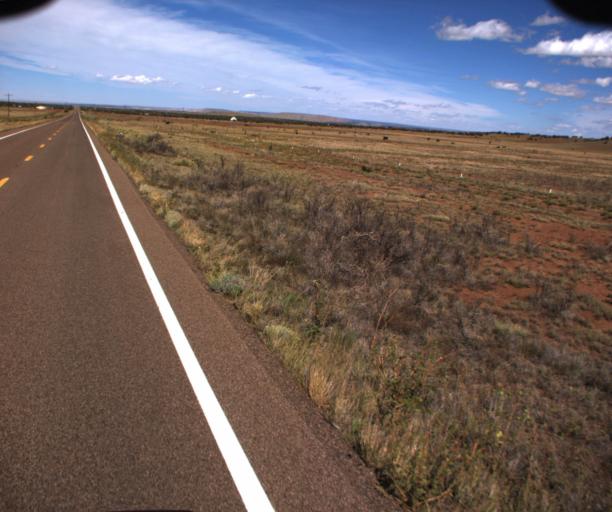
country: US
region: Arizona
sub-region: Apache County
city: Saint Johns
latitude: 34.5049
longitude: -109.6212
